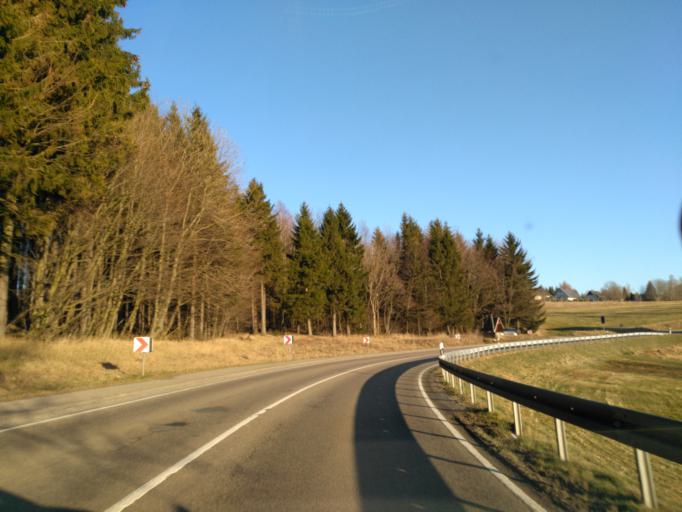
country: DE
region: Saxony
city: Annaberg-Buchholz
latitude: 50.5710
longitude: 13.0125
